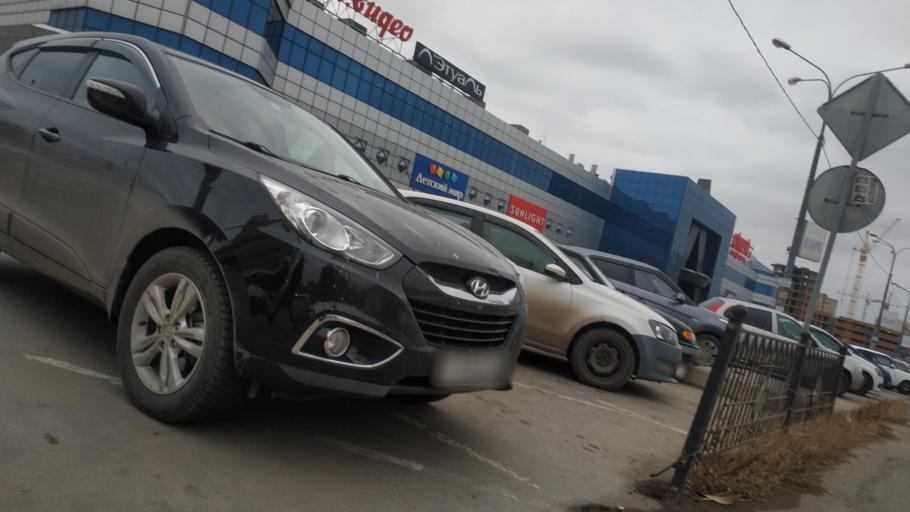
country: RU
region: Astrakhan
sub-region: Gorod Astrakhan'
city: Astrakhan'
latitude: 46.3399
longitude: 48.0252
